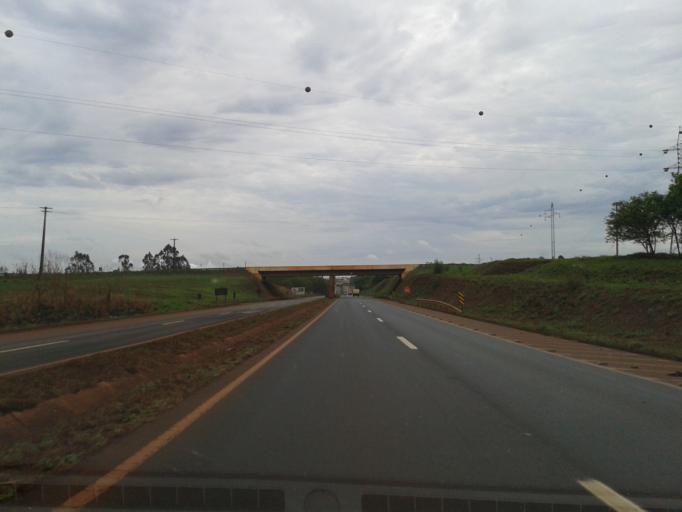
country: BR
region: Goias
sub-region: Itumbiara
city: Itumbiara
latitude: -18.4538
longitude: -49.1879
